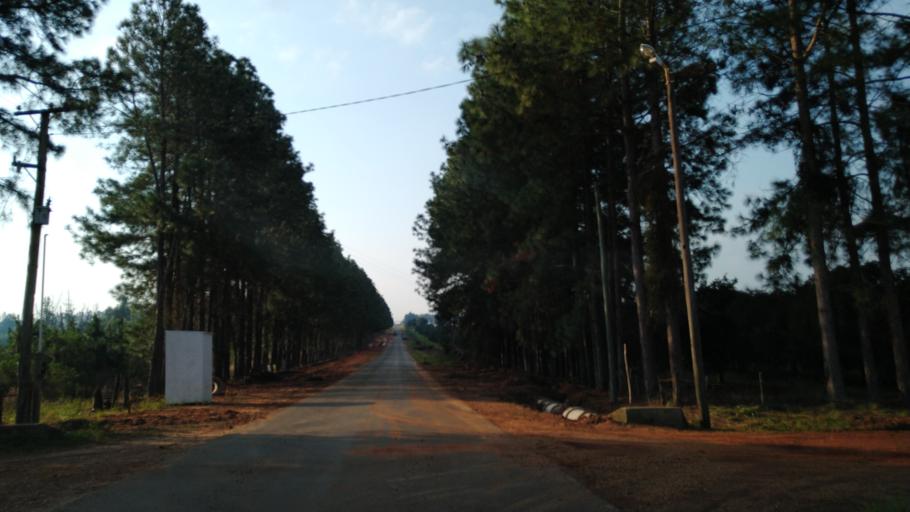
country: AR
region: Entre Rios
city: Santa Ana
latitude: -30.9093
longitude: -57.9261
